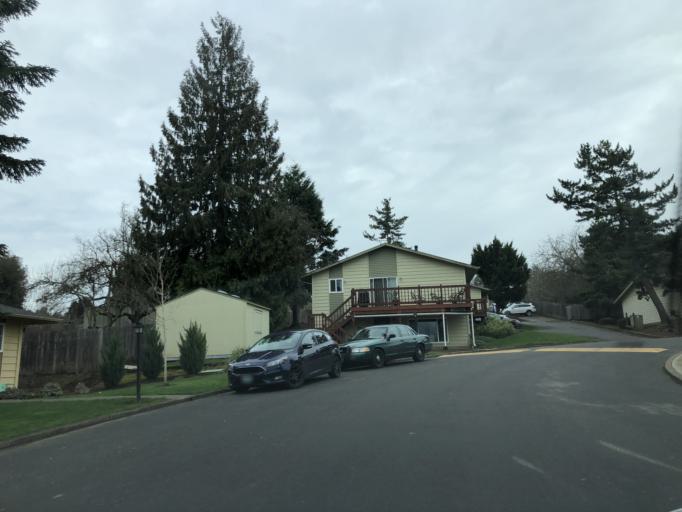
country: US
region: Oregon
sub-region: Washington County
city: Tigard
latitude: 45.4182
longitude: -122.7821
